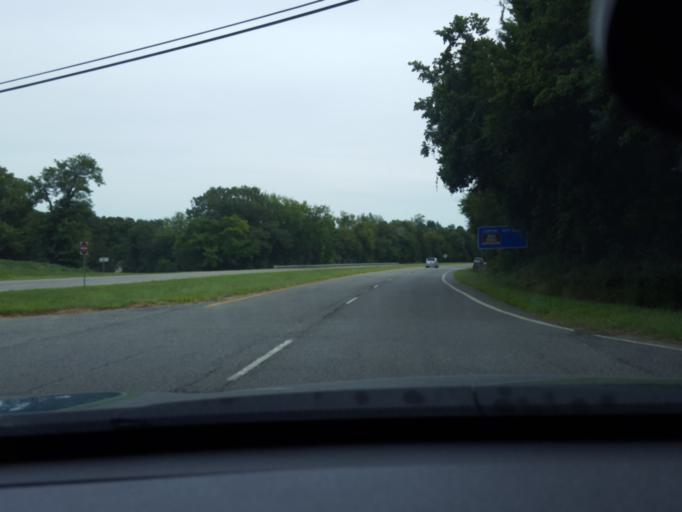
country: US
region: Virginia
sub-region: Caroline County
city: Bowling Green
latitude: 38.0504
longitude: -77.3410
